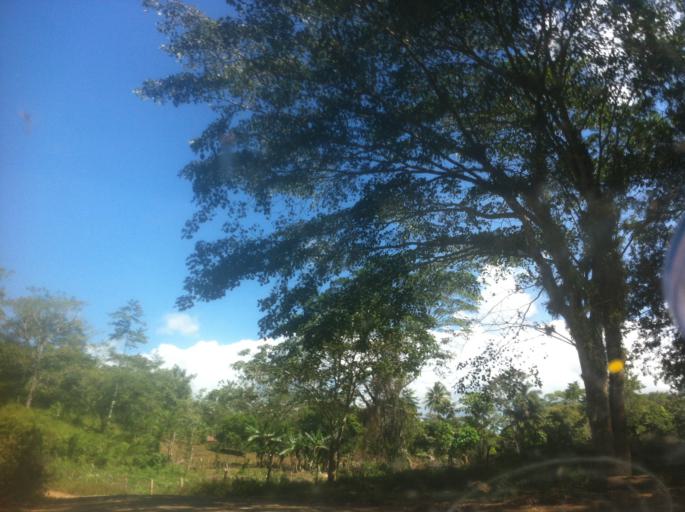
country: CR
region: Alajuela
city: Los Chiles
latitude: 11.2507
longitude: -84.4419
